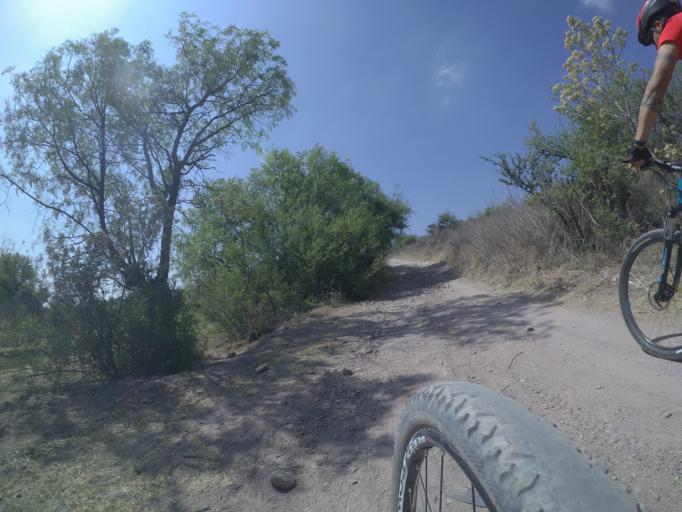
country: MX
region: Aguascalientes
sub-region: Jesus Maria
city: Paseos de las Haciendas [Fraccionamiento]
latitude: 22.0015
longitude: -102.3684
